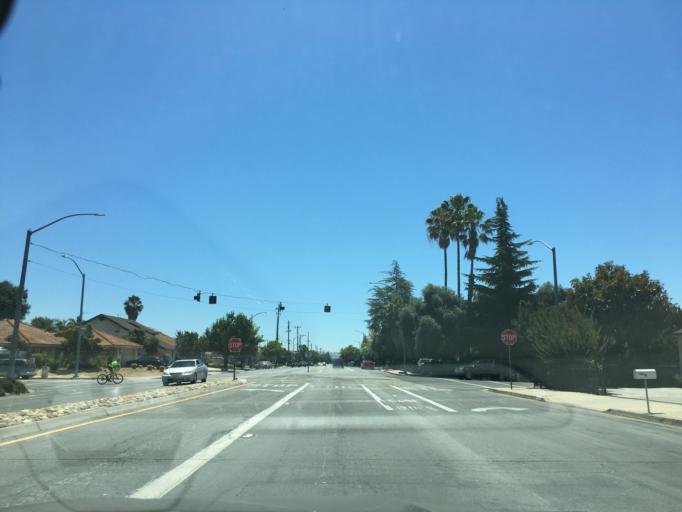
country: US
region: California
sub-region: Santa Clara County
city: Alum Rock
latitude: 37.3842
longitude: -121.8427
